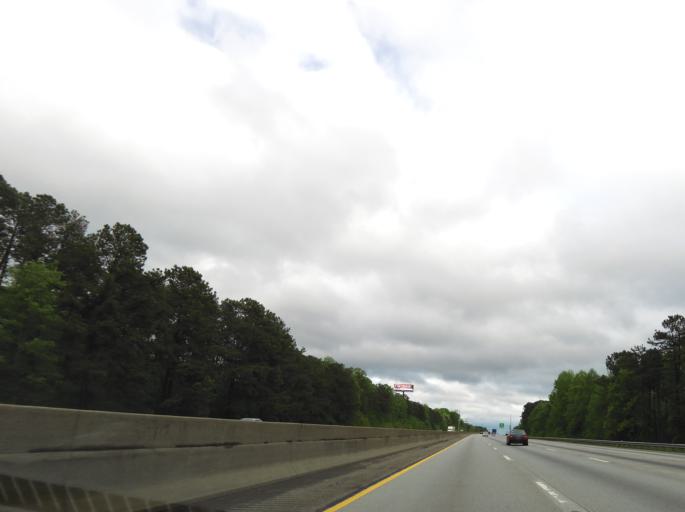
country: US
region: Georgia
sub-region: Clayton County
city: Morrow
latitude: 33.5536
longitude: -84.2964
